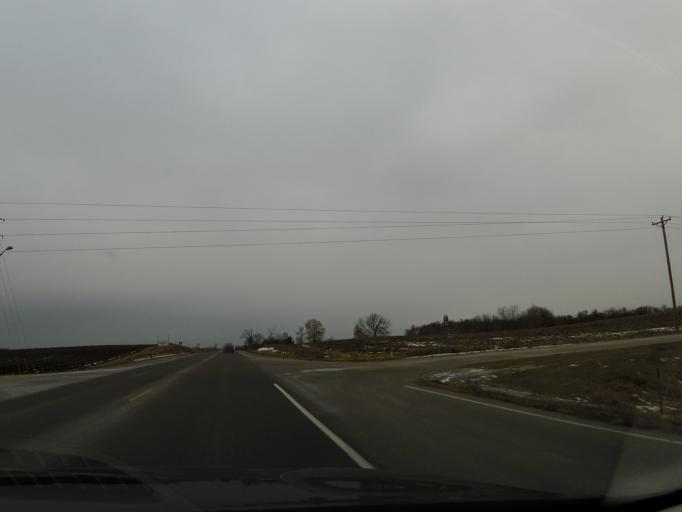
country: US
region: Minnesota
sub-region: Carver County
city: Cologne
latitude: 44.7678
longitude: -93.8284
